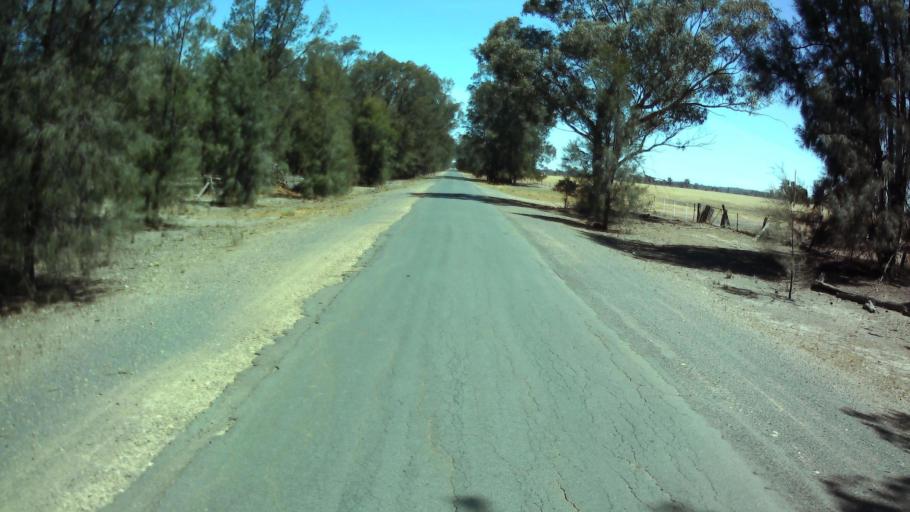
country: AU
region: New South Wales
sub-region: Weddin
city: Grenfell
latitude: -33.8796
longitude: 147.6903
